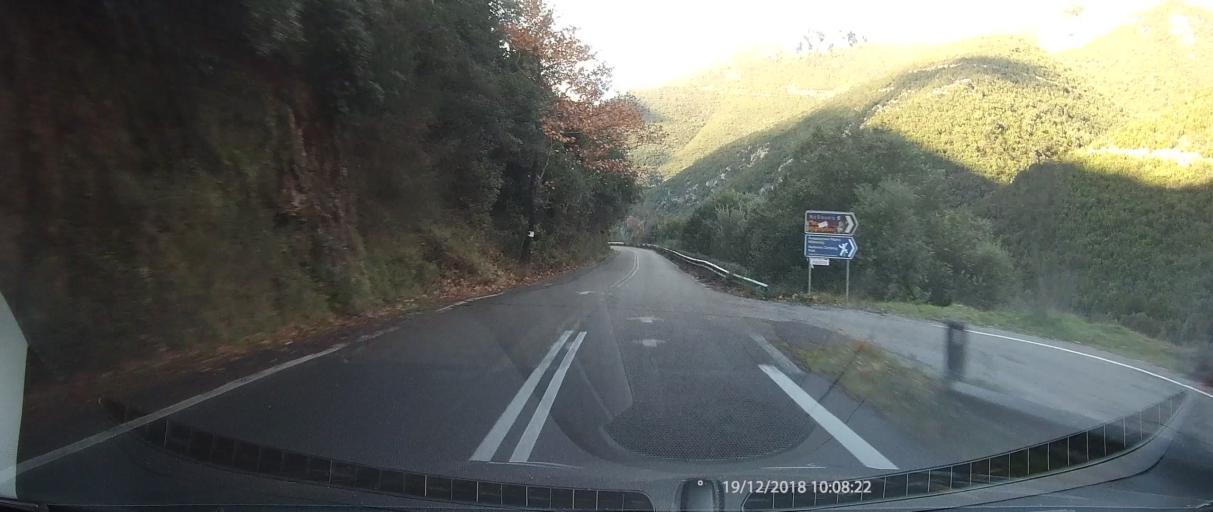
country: GR
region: Peloponnese
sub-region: Nomos Messinias
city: Paralia Vergas
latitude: 37.1153
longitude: 22.2026
